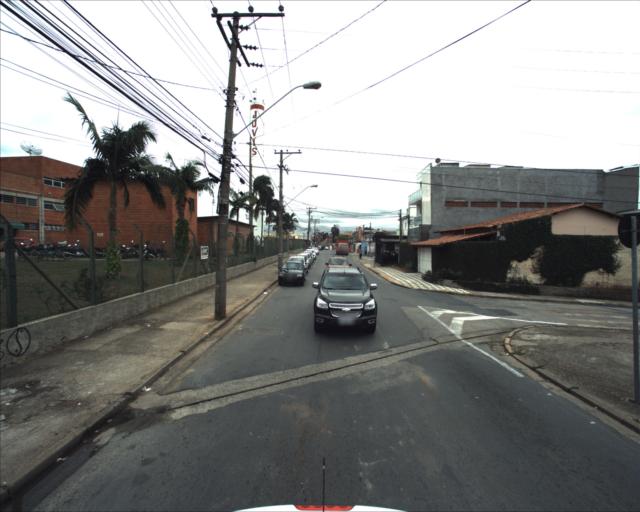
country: BR
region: Sao Paulo
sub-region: Sorocaba
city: Sorocaba
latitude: -23.4752
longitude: -47.4722
